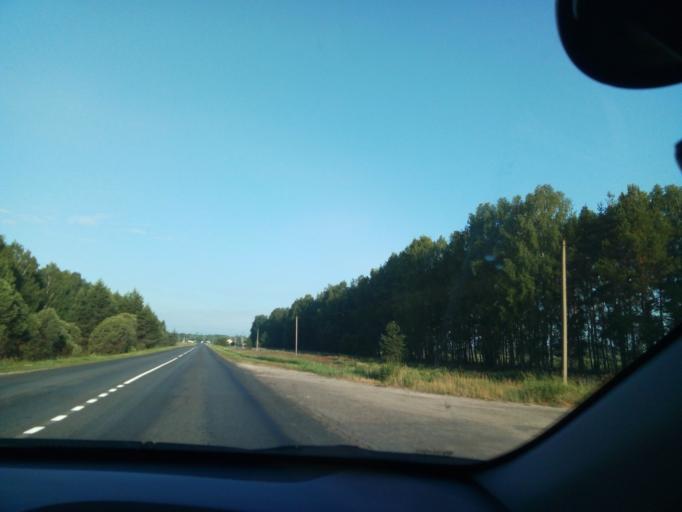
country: RU
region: Nizjnij Novgorod
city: Voznesenskoye
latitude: 54.8581
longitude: 42.9058
